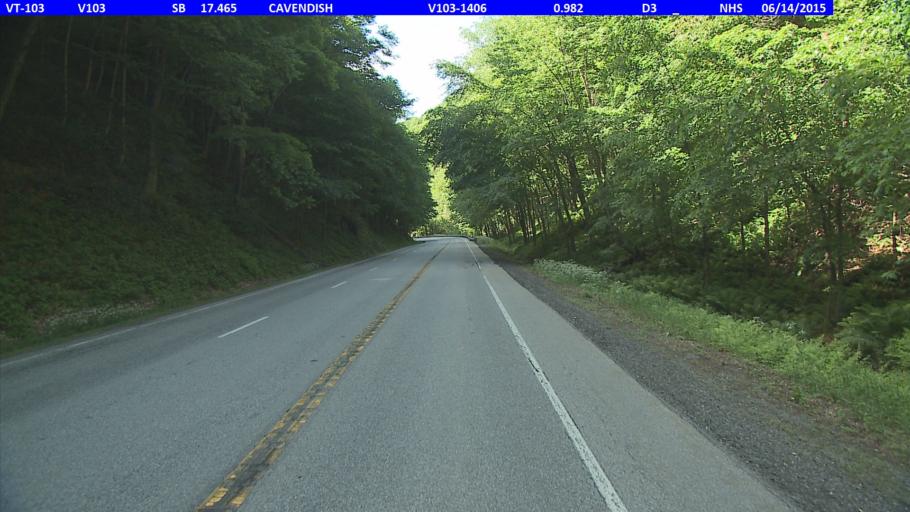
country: US
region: Vermont
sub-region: Windsor County
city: Chester
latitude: 43.3610
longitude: -72.6339
